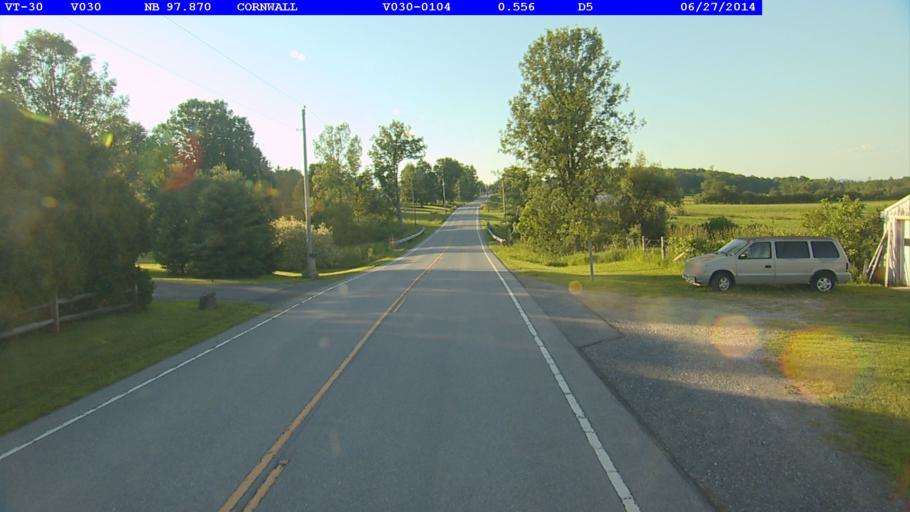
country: US
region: Vermont
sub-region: Addison County
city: Middlebury (village)
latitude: 43.9159
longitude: -73.2098
